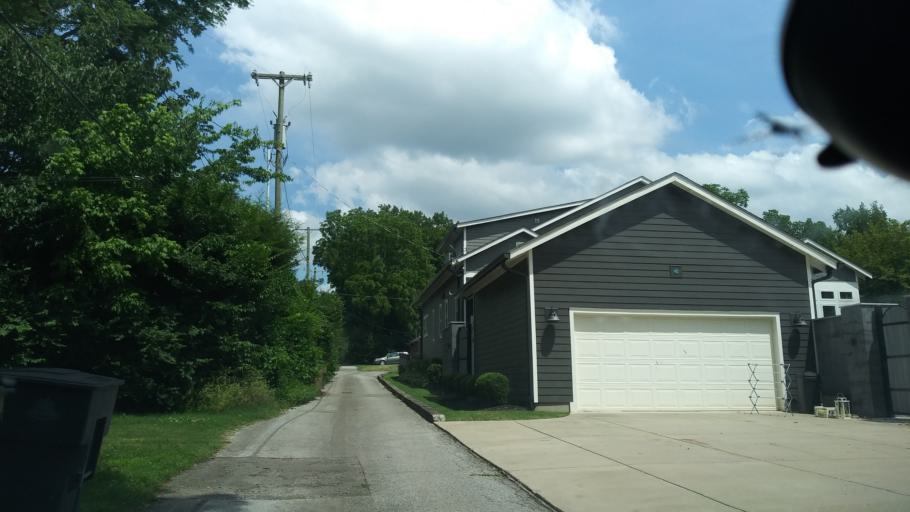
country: US
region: Tennessee
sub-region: Davidson County
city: Belle Meade
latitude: 36.1418
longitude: -86.8380
